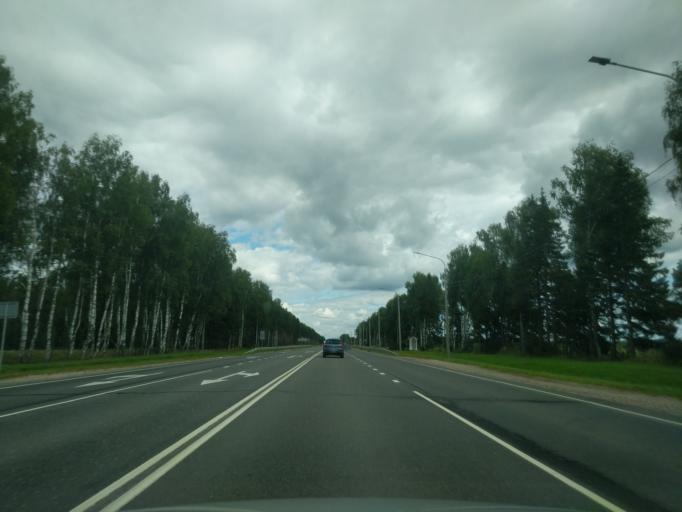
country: RU
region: Jaroslavl
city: Nekrasovskoye
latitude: 57.6090
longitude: 40.3334
